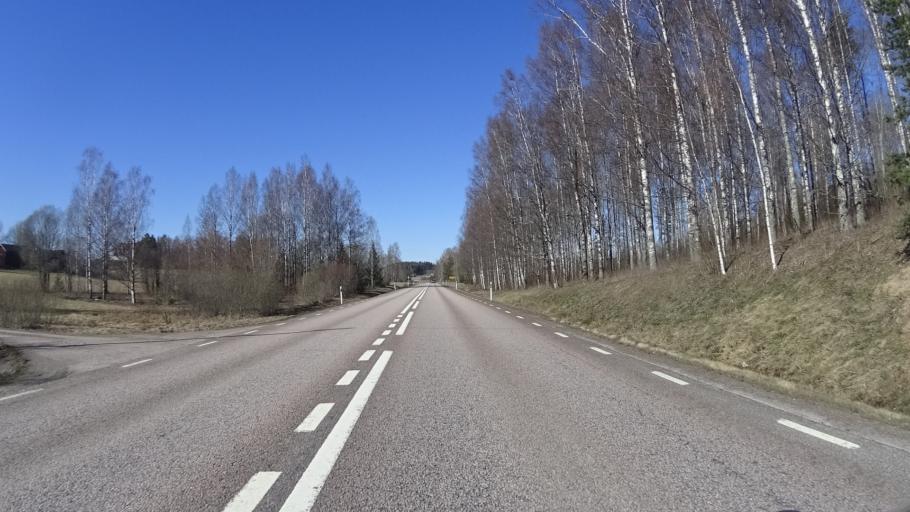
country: SE
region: Vaermland
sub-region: Karlstads Kommun
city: Edsvalla
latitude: 59.5708
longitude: 13.0219
